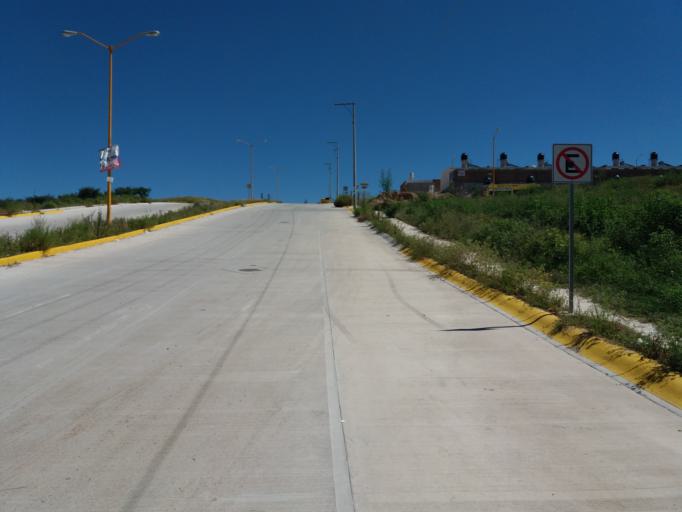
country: MX
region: Aguascalientes
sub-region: Aguascalientes
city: Aguascalientes
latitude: 21.8686
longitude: -102.2313
